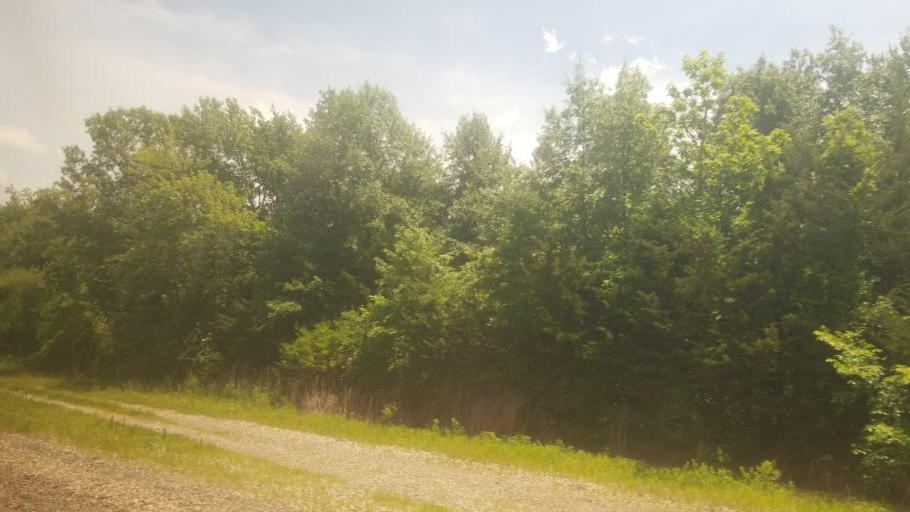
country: US
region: Missouri
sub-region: Macon County
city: La Plata
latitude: 40.0302
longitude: -92.4881
